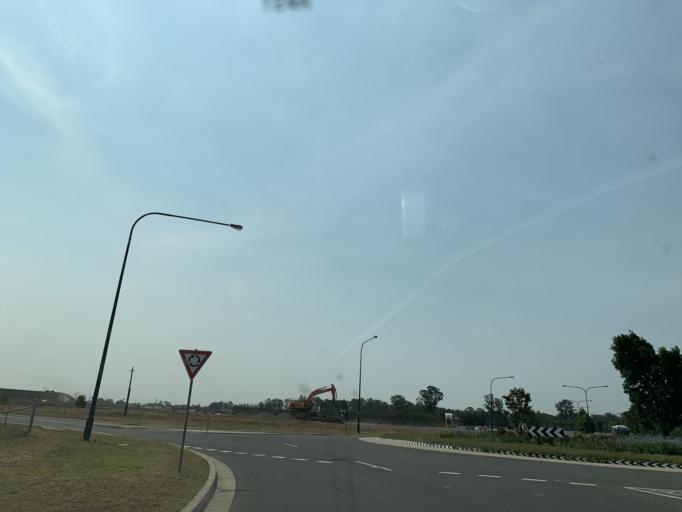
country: AU
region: New South Wales
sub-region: Blacktown
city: Hassall Grove
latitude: -33.7168
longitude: 150.8351
